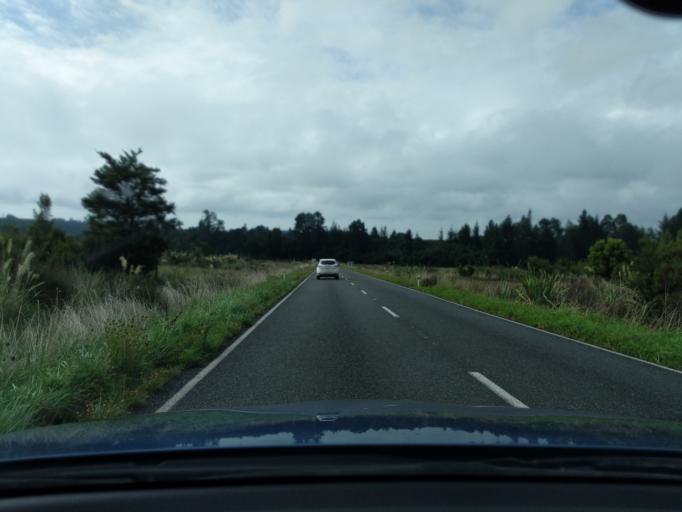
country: NZ
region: Tasman
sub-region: Tasman District
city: Takaka
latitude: -40.6793
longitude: 172.6646
